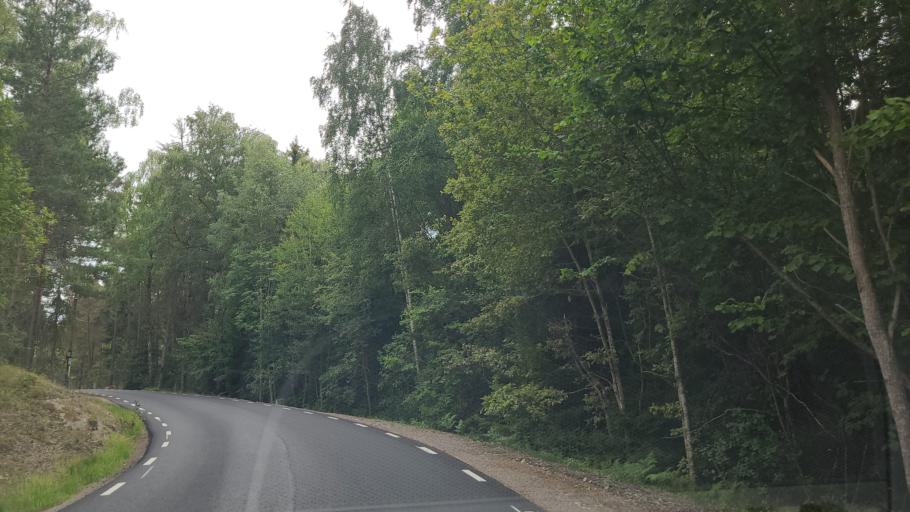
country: SE
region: Stockholm
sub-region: Upplands-Bro Kommun
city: Bro
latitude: 59.4822
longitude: 17.5989
